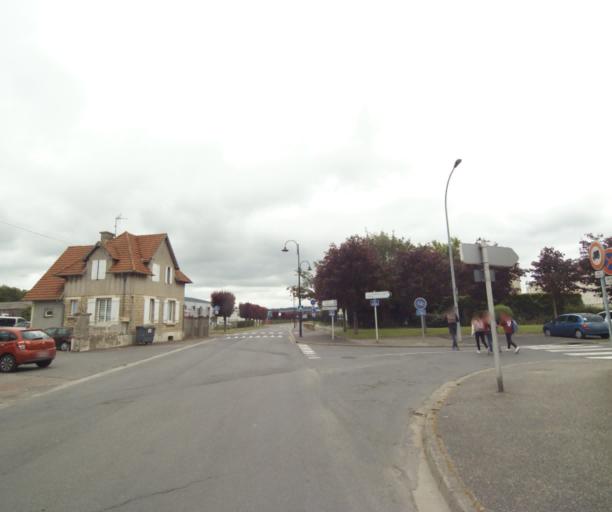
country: FR
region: Lower Normandy
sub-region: Departement du Calvados
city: Dives-sur-Mer
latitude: 49.2810
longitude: -0.0959
